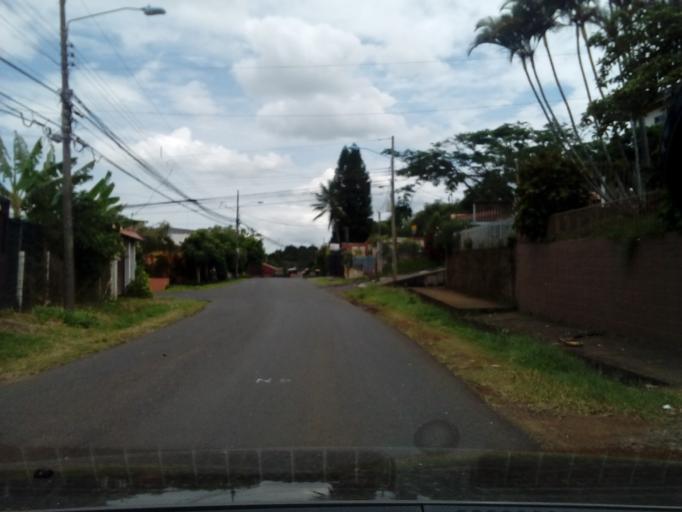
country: CR
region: Heredia
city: San Josecito
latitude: 10.0180
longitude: -84.0968
